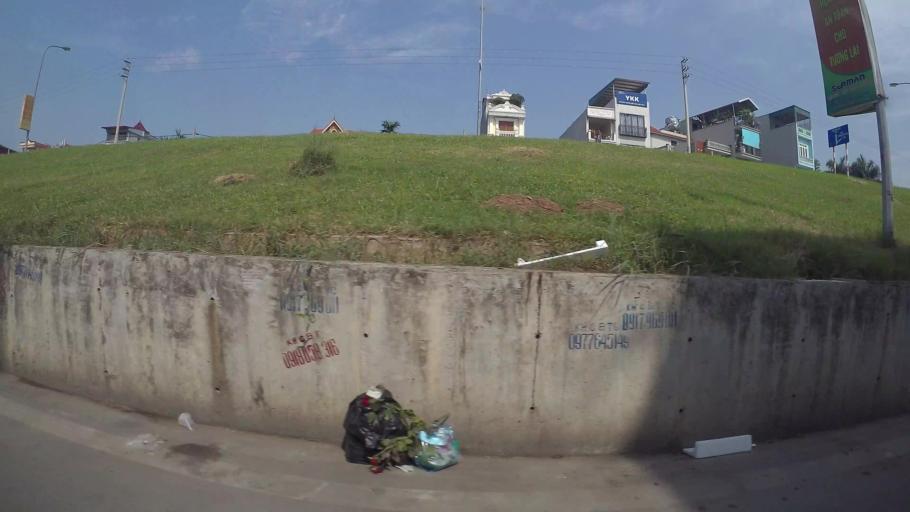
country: VN
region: Ha Noi
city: Hoan Kiem
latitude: 21.0536
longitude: 105.8642
